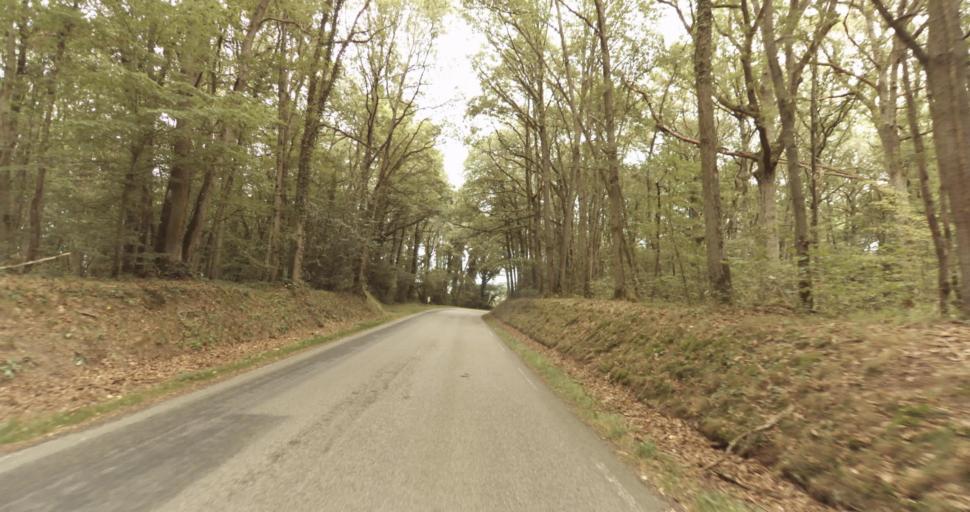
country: FR
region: Haute-Normandie
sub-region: Departement de l'Eure
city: Menilles
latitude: 49.0419
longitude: 1.3049
